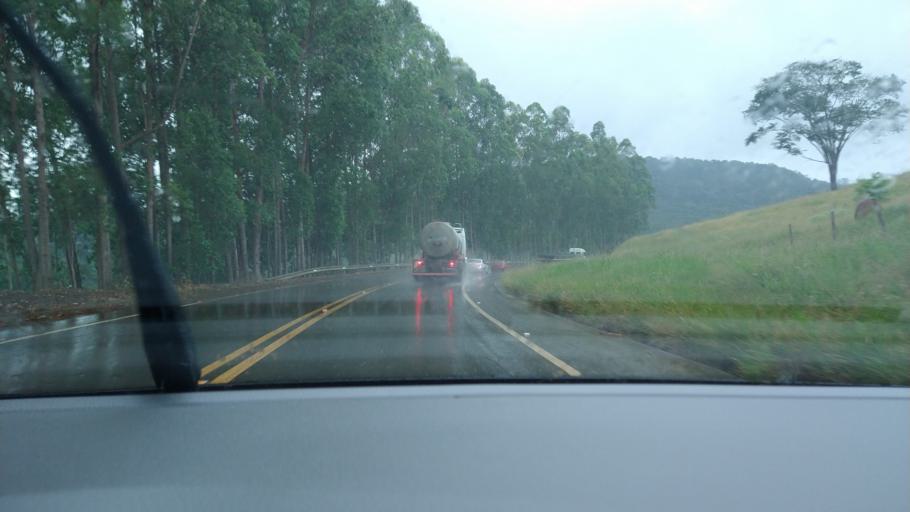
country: BR
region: Minas Gerais
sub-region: Vicosa
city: Vicosa
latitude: -20.5926
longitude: -42.8811
